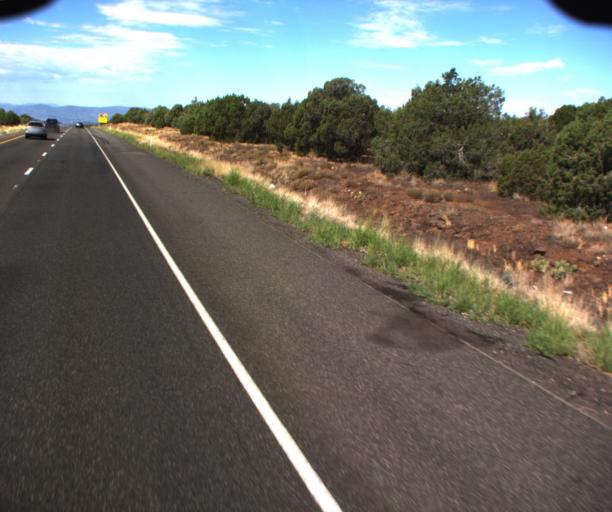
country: US
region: Arizona
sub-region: Yavapai County
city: Big Park
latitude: 34.7338
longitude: -111.7012
